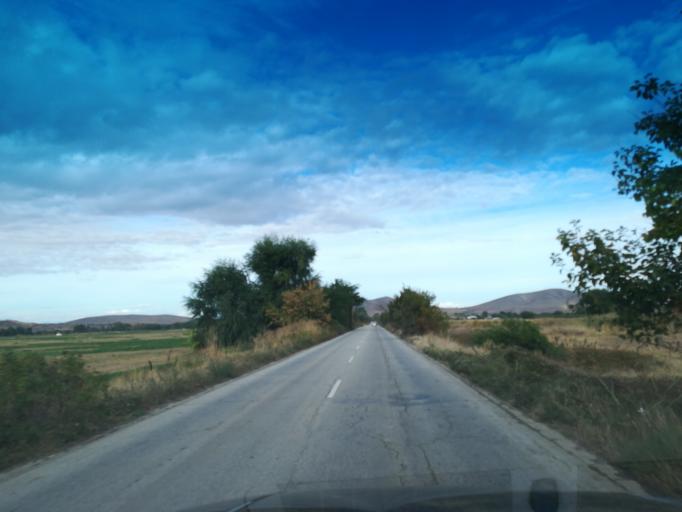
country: BG
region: Plovdiv
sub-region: Obshtina Krichim
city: Krichim
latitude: 42.0755
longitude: 24.4113
